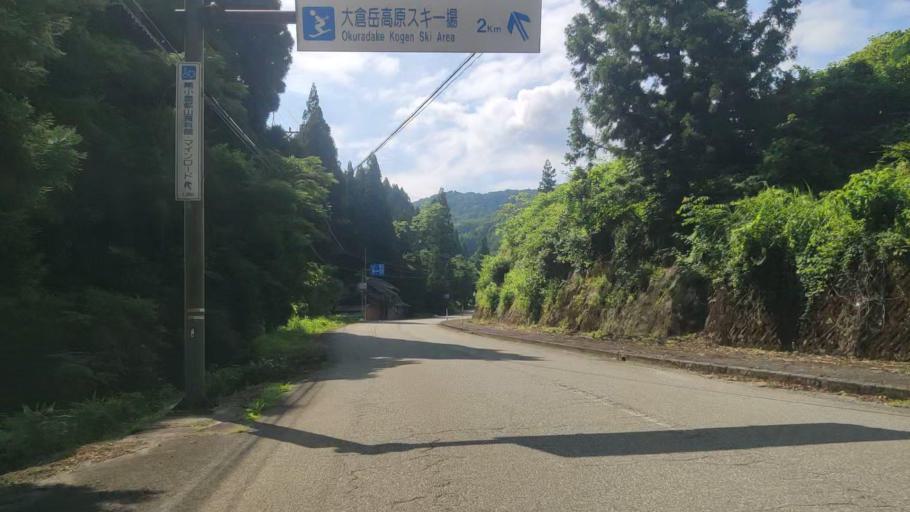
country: JP
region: Ishikawa
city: Komatsu
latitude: 36.3009
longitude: 136.5283
